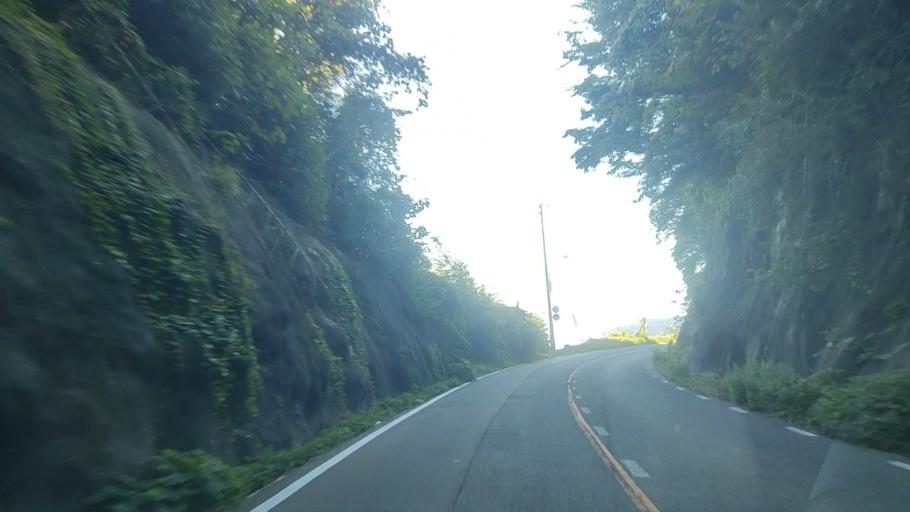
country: JP
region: Ishikawa
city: Nanao
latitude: 37.2734
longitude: 137.0970
